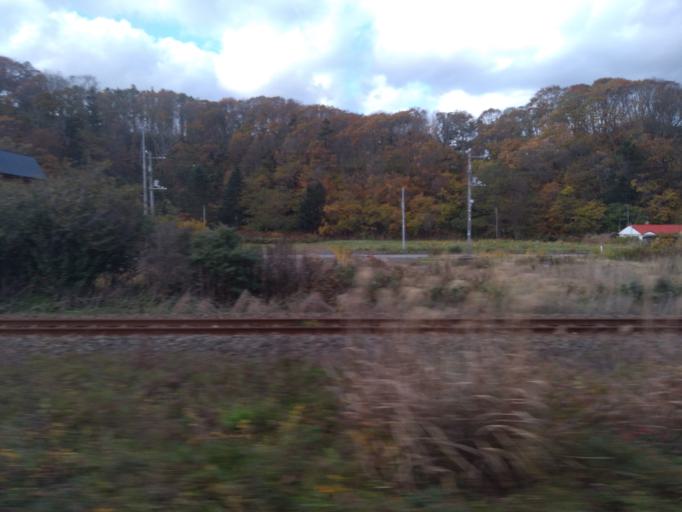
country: JP
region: Hokkaido
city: Niseko Town
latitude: 42.5844
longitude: 140.6342
